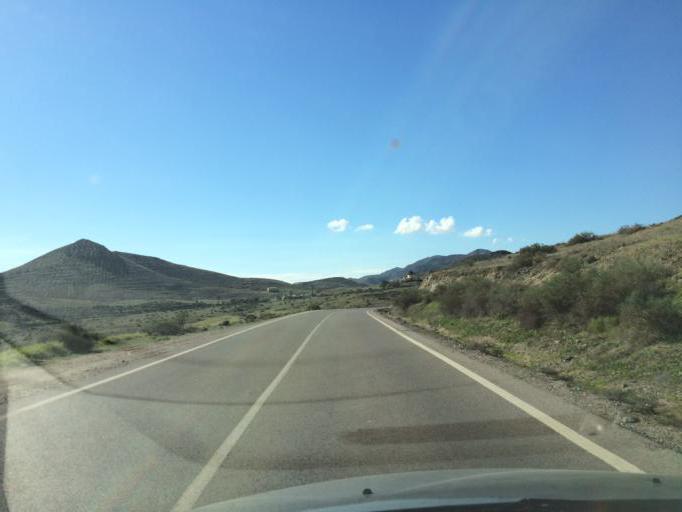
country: ES
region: Andalusia
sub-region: Provincia de Almeria
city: San Jose
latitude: 36.8025
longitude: -2.0925
